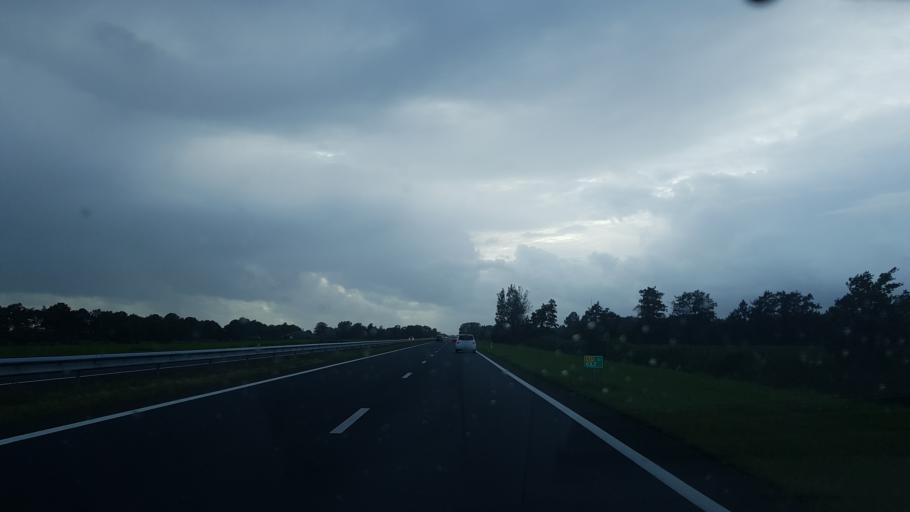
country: NL
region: Friesland
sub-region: Gemeente Tytsjerksteradiel
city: Garyp
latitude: 53.1491
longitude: 5.9841
